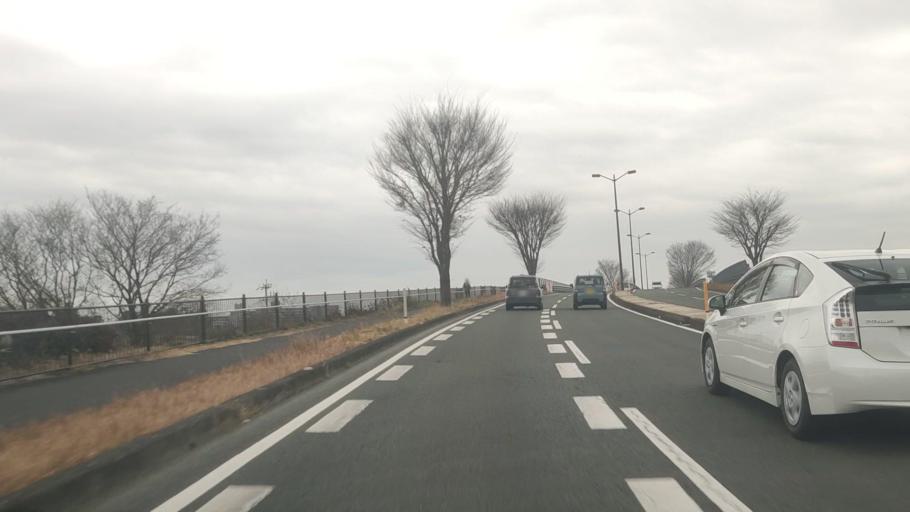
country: JP
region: Kumamoto
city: Ozu
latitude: 32.8198
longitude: 130.7903
